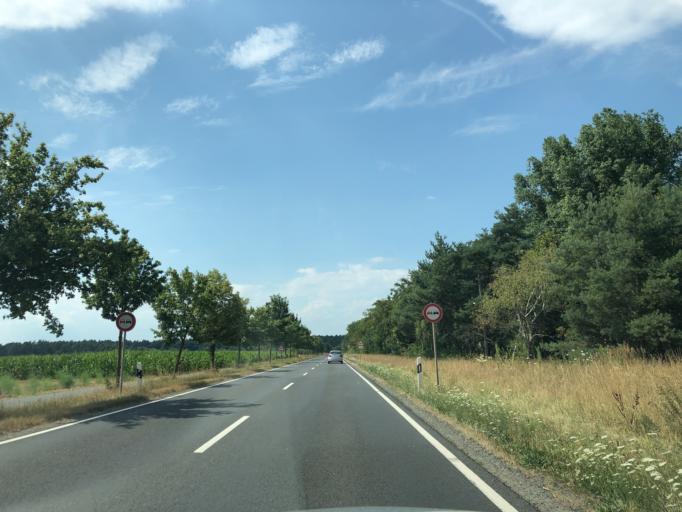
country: DE
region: Hesse
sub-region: Regierungsbezirk Darmstadt
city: Babenhausen
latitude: 49.9734
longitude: 8.9414
